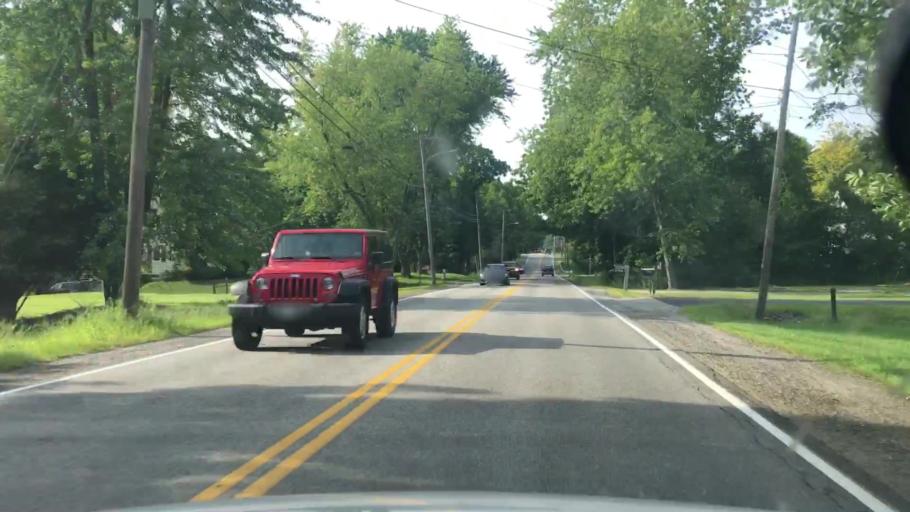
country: US
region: Maine
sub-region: Cumberland County
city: Westbrook
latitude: 43.7318
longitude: -70.3450
